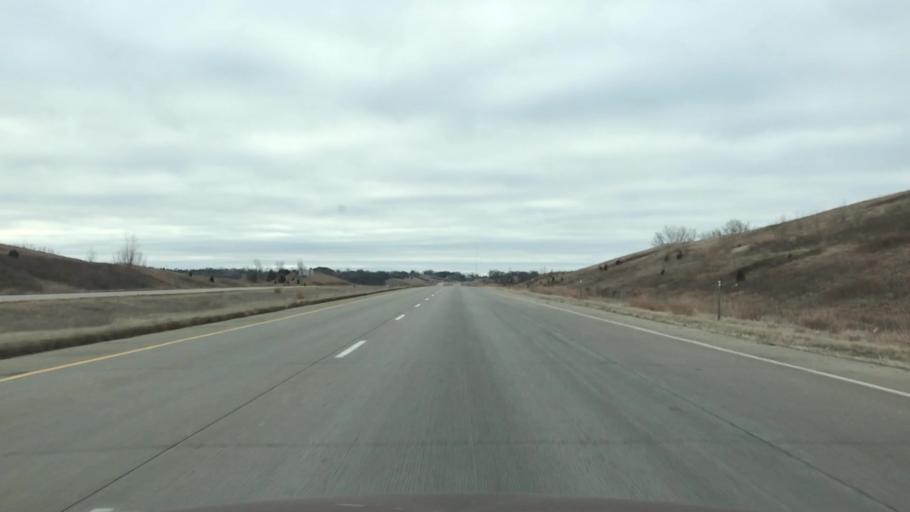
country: US
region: Iowa
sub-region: Woodbury County
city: Sioux City
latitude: 42.5141
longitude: -96.3349
